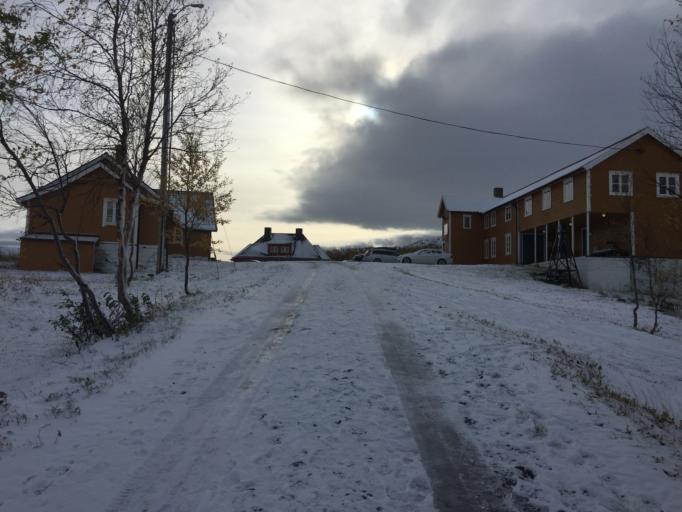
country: NO
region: Nordland
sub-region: Sorfold
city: Straumen
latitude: 67.0951
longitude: 16.0059
